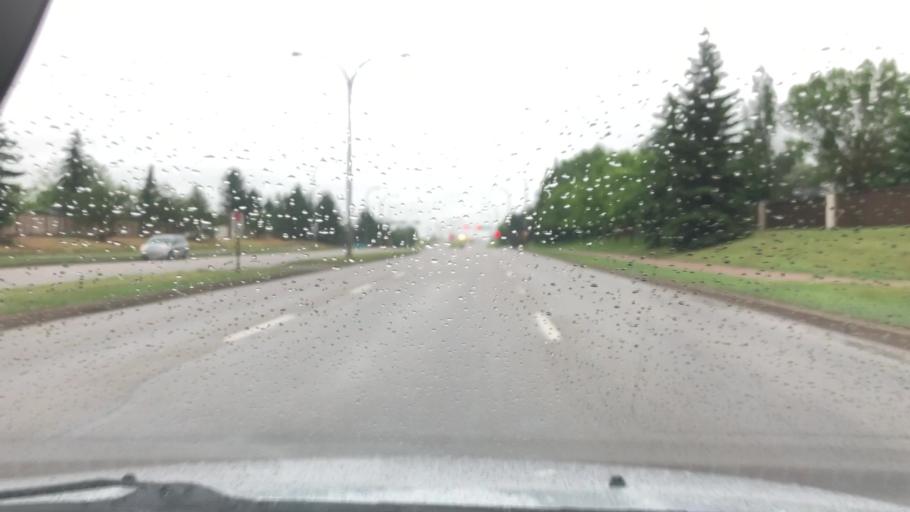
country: CA
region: Alberta
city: Sherwood Park
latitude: 53.5411
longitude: -113.2585
